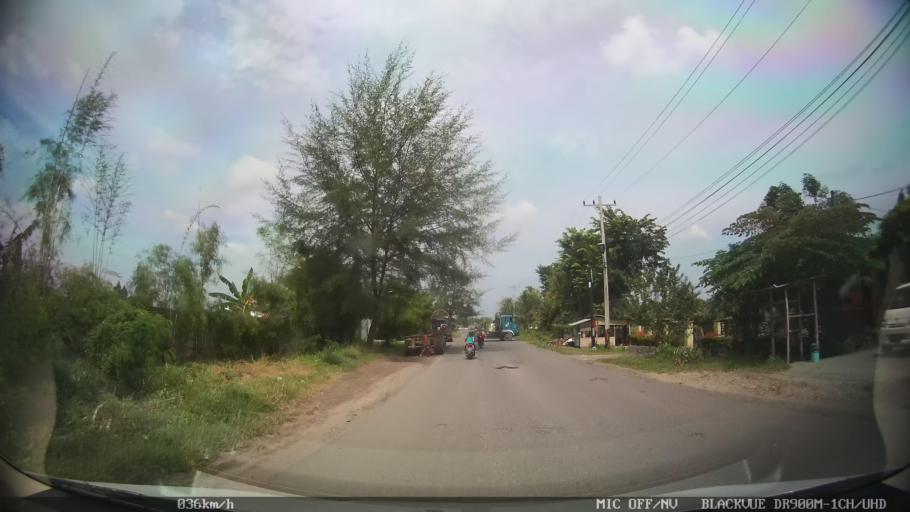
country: ID
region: North Sumatra
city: Medan
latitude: 3.6504
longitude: 98.7160
